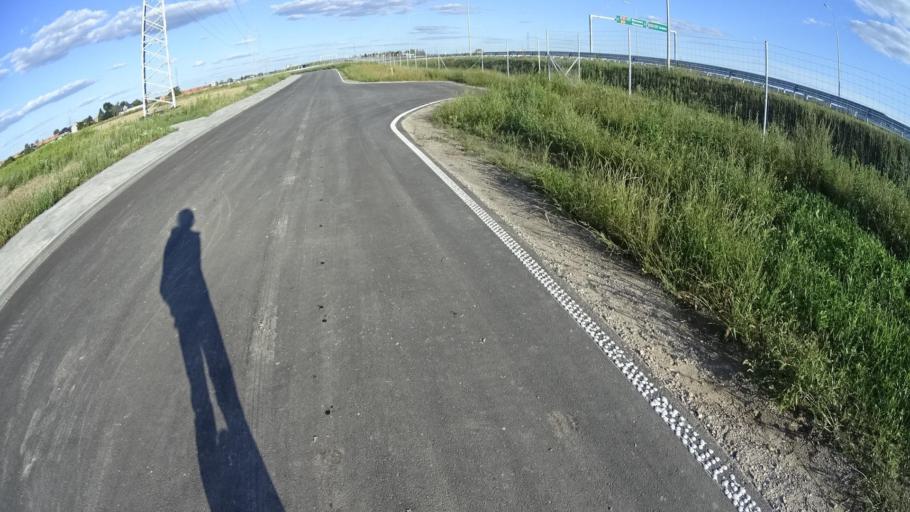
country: PL
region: Masovian Voivodeship
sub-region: Powiat piaseczynski
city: Lesznowola
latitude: 52.0912
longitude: 20.9631
